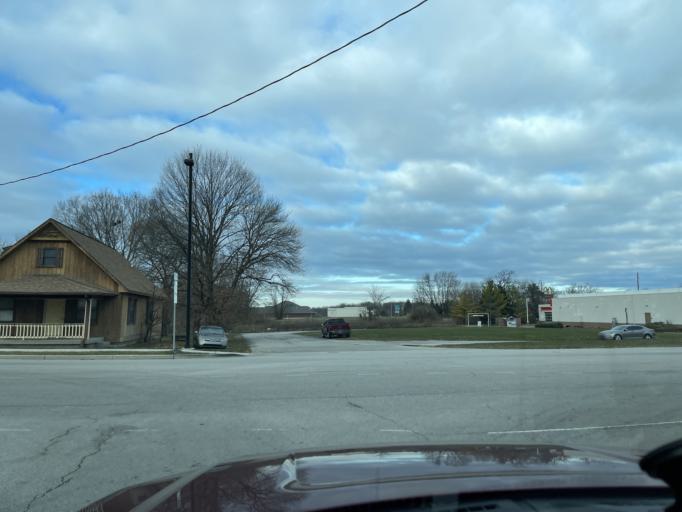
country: US
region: Indiana
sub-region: Hendricks County
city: Avon
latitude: 39.7617
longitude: -86.3993
